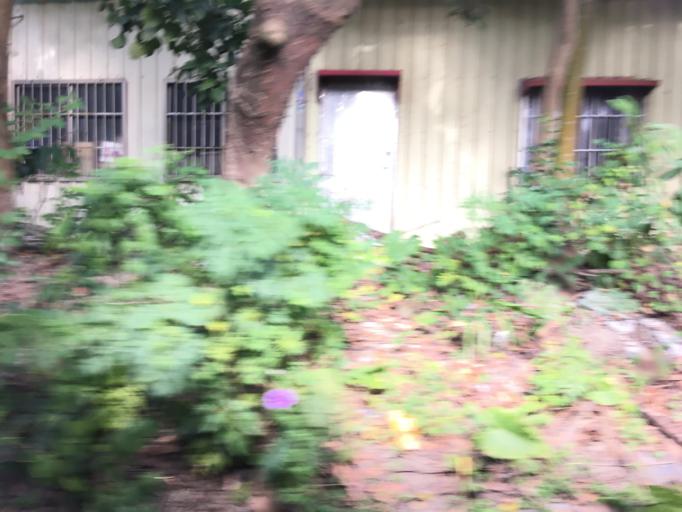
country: TW
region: Taiwan
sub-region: Chiayi
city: Jiayi Shi
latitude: 23.4927
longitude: 120.5015
